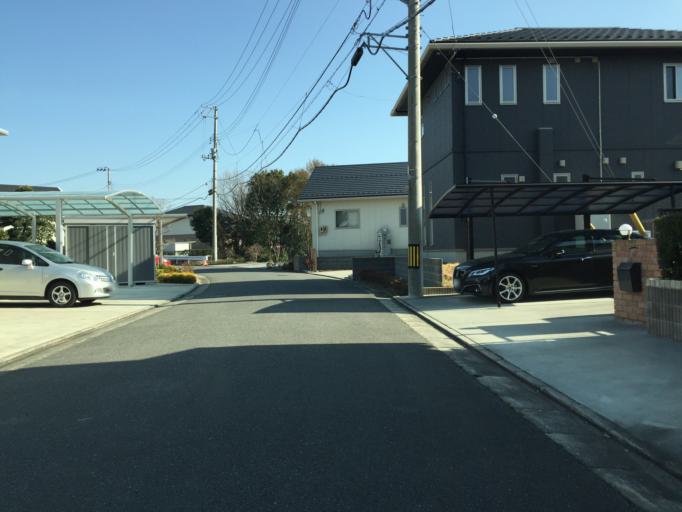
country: JP
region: Fukushima
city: Iwaki
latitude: 36.9618
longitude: 140.8673
